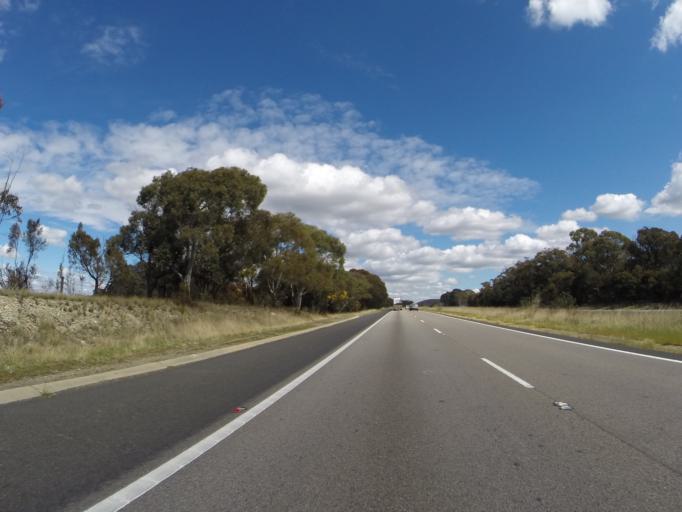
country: AU
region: New South Wales
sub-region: Goulburn Mulwaree
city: Goulburn
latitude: -34.7380
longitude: 149.9468
